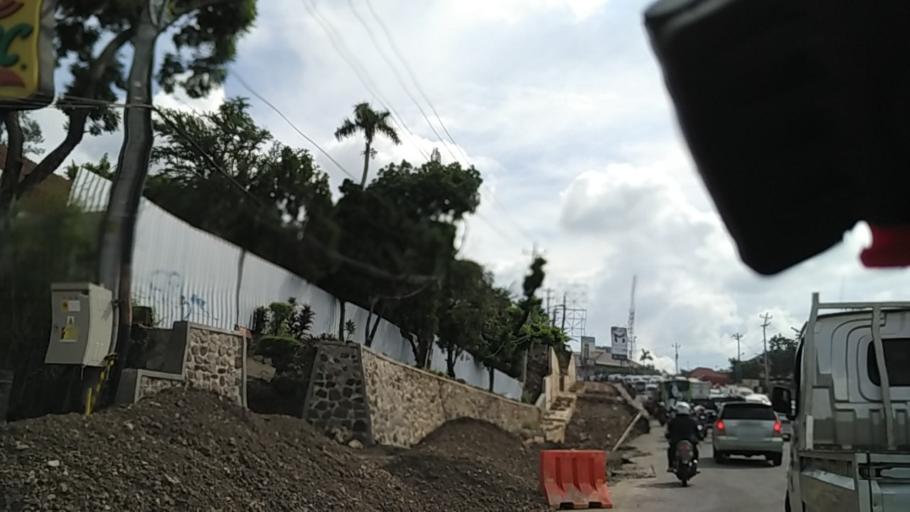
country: ID
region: Central Java
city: Semarang
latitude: -7.0246
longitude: 110.4198
